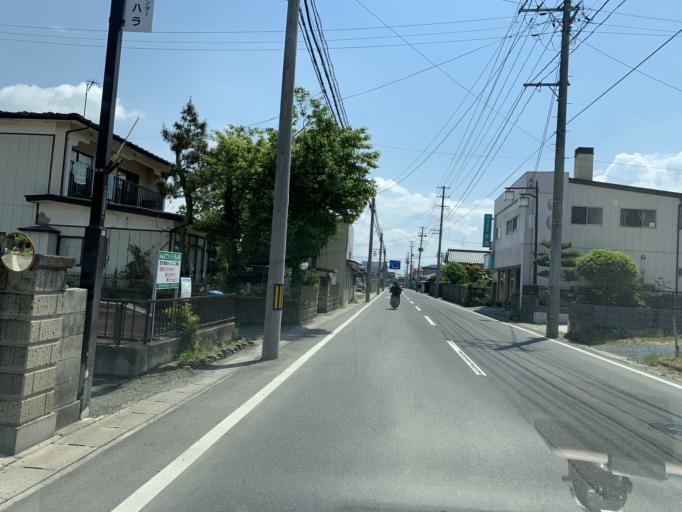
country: JP
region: Miyagi
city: Kogota
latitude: 38.5596
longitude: 141.0532
